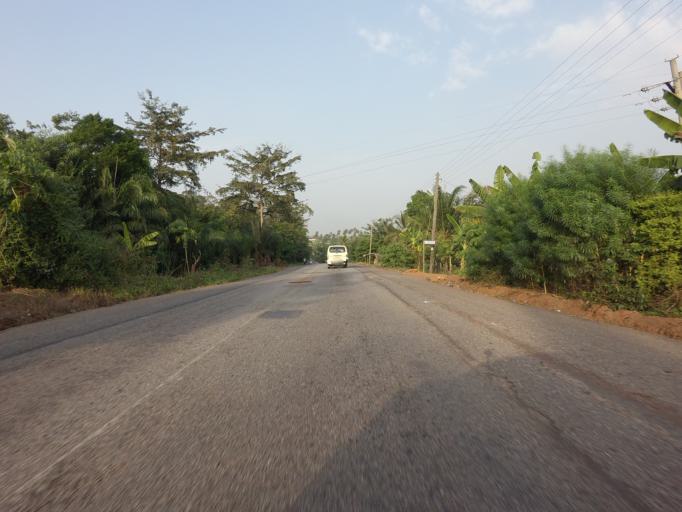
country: GH
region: Volta
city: Ho
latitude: 6.5317
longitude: 0.2804
